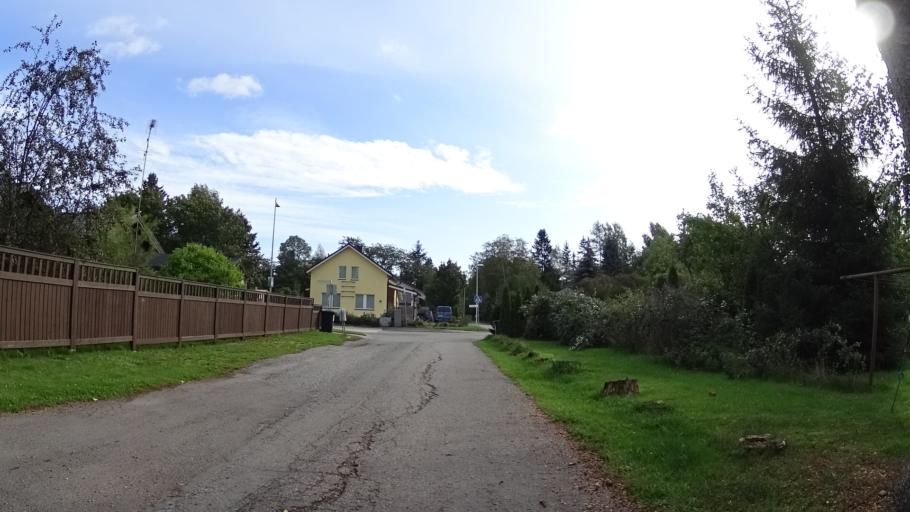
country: FI
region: Uusimaa
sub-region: Helsinki
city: Vantaa
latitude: 60.2961
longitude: 25.0038
